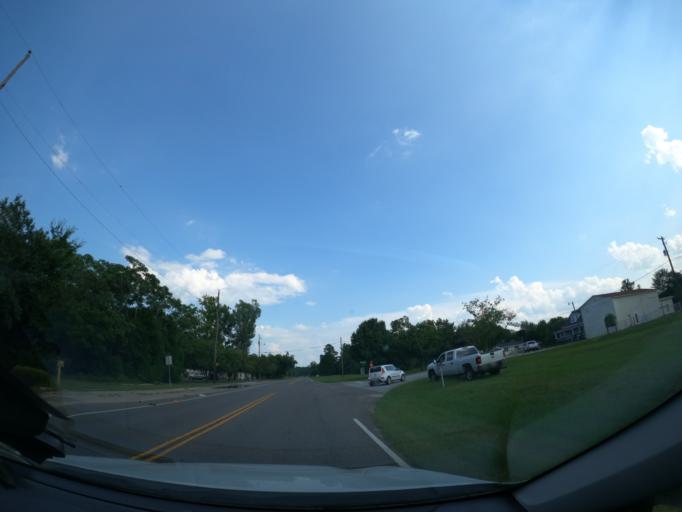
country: US
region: South Carolina
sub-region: Barnwell County
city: Williston
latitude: 33.4809
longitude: -81.5125
